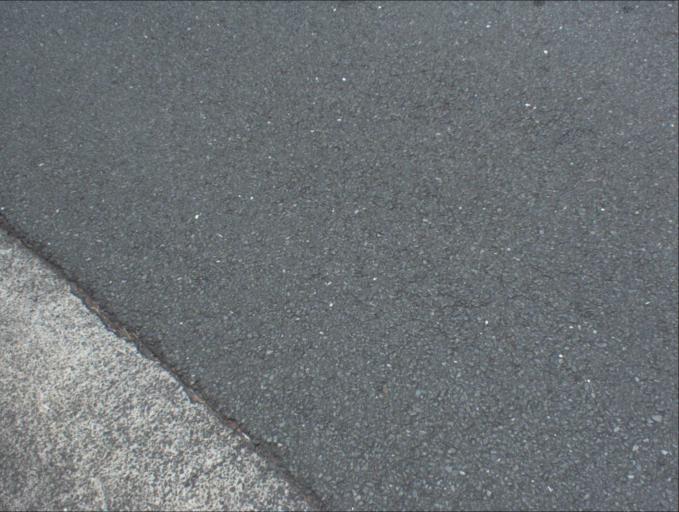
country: AU
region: Queensland
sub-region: Logan
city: Beenleigh
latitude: -27.6706
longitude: 153.1973
